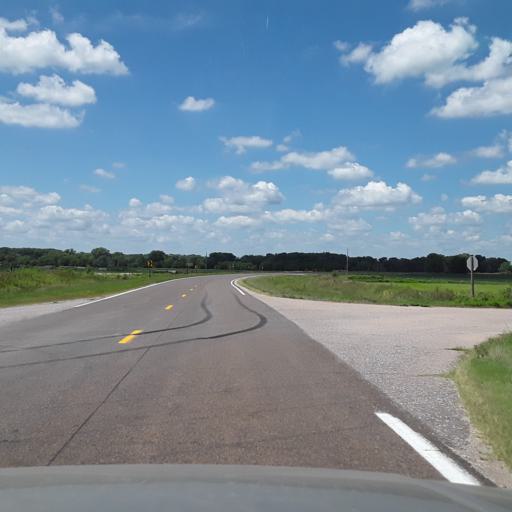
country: US
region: Nebraska
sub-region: Nance County
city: Genoa
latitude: 41.4077
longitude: -97.7145
